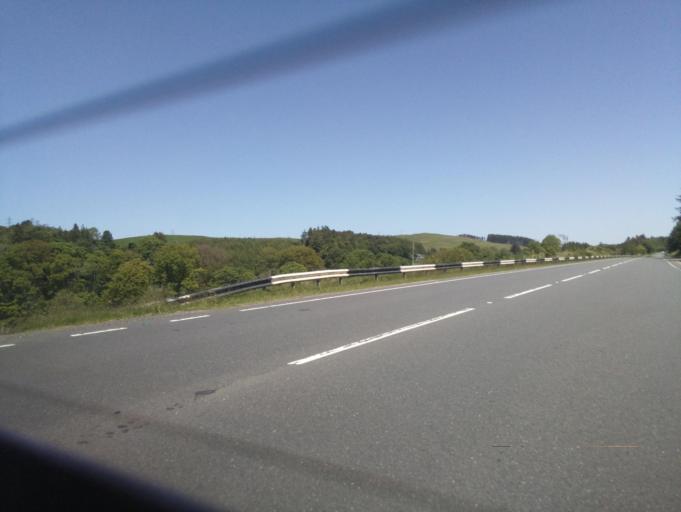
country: GB
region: Scotland
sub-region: The Scottish Borders
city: Hawick
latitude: 55.3544
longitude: -2.9110
